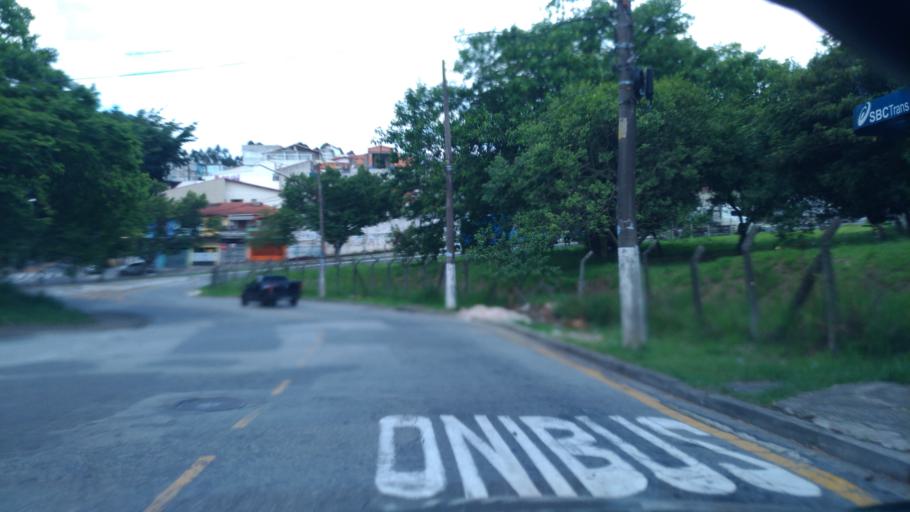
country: BR
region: Sao Paulo
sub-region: Sao Bernardo Do Campo
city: Sao Bernardo do Campo
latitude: -23.7053
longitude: -46.5823
